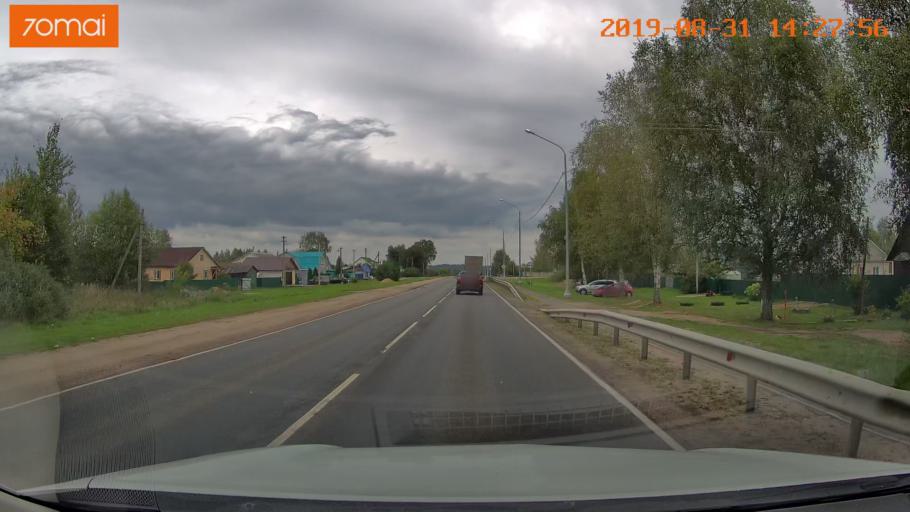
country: RU
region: Smolensk
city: Yekimovichi
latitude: 54.1182
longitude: 33.3063
